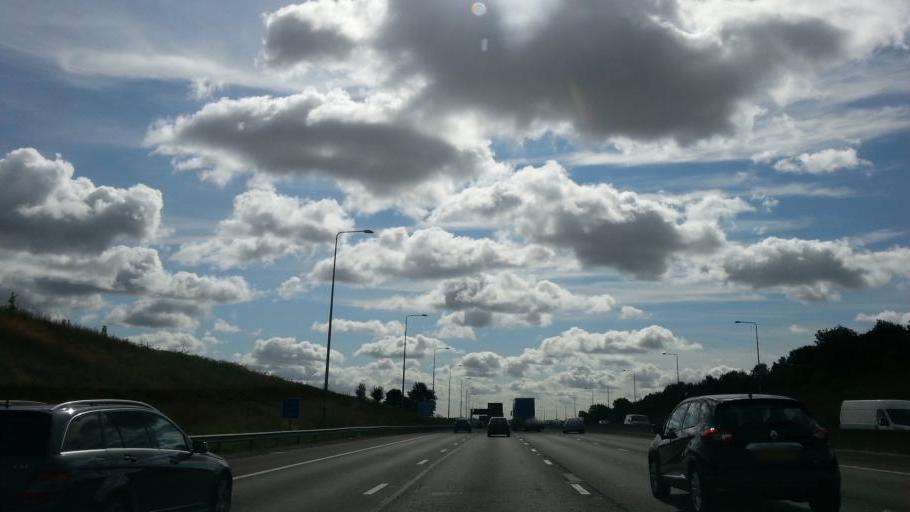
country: GB
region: England
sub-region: Hertfordshire
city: Shenley AV
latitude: 51.7079
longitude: -0.2574
